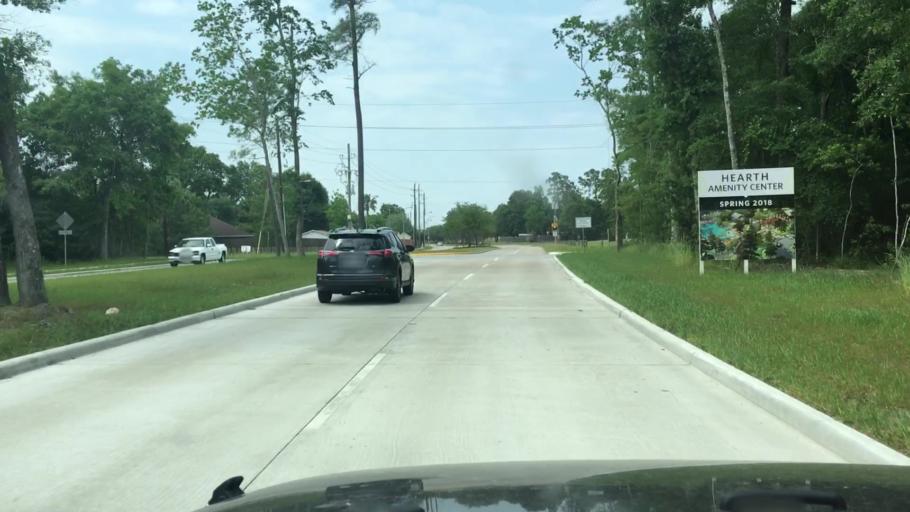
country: US
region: Texas
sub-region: Harris County
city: Atascocita
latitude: 29.9628
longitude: -95.2101
